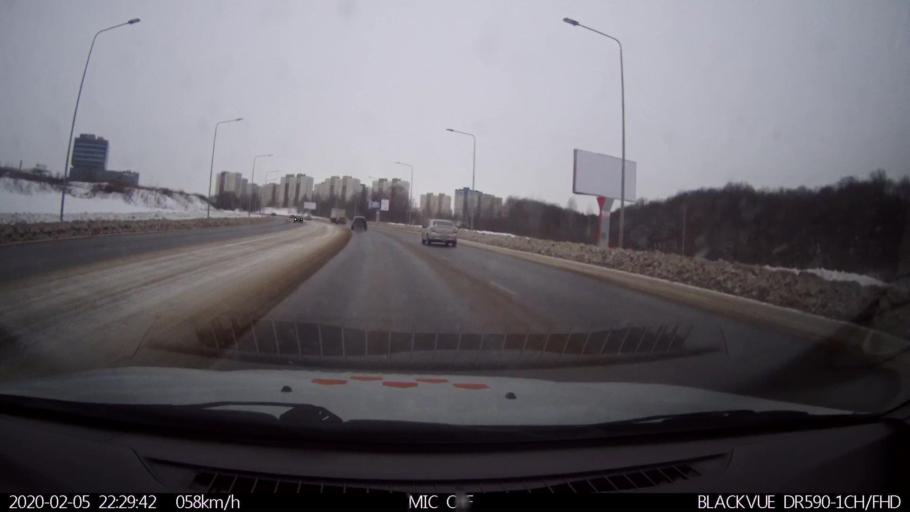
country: RU
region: Nizjnij Novgorod
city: Imeni Stepana Razina
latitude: 54.7474
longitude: 44.1477
